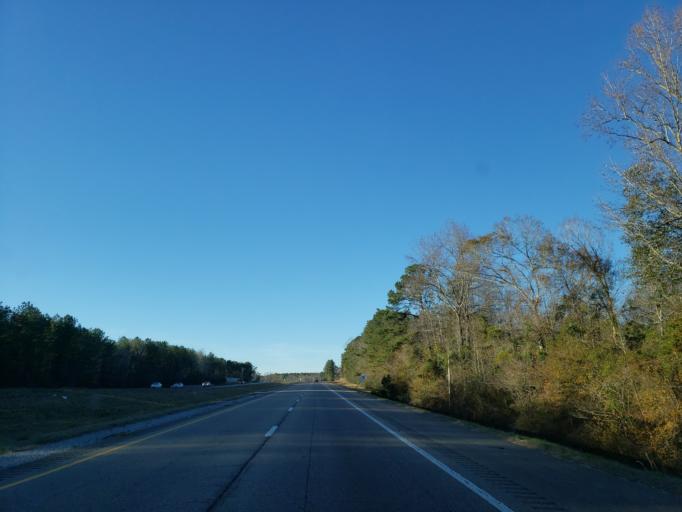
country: US
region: Mississippi
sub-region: Lamar County
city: Sumrall
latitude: 31.4750
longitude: -89.4562
